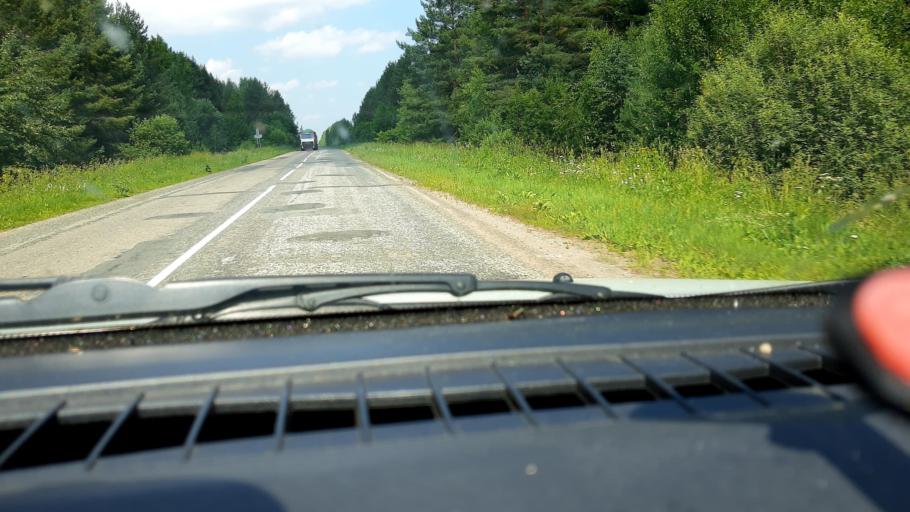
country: RU
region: Nizjnij Novgorod
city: Sharanga
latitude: 57.1047
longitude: 46.5296
